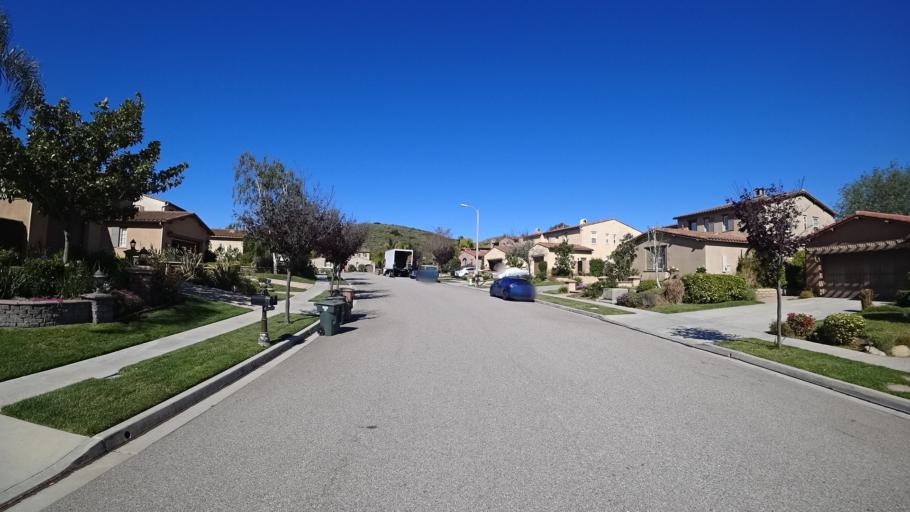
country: US
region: California
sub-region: Ventura County
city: Casa Conejo
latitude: 34.1736
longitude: -118.9874
